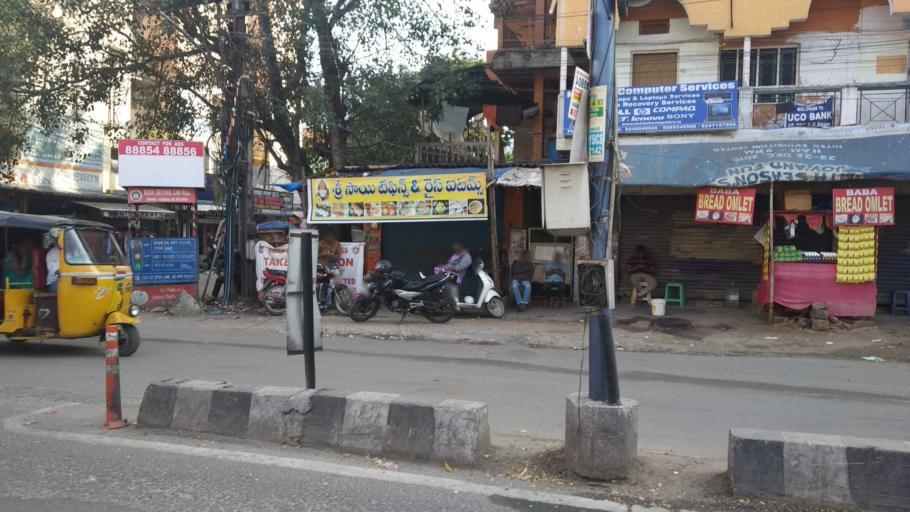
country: IN
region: Telangana
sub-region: Rangareddi
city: Kukatpalli
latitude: 17.4419
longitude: 78.4455
